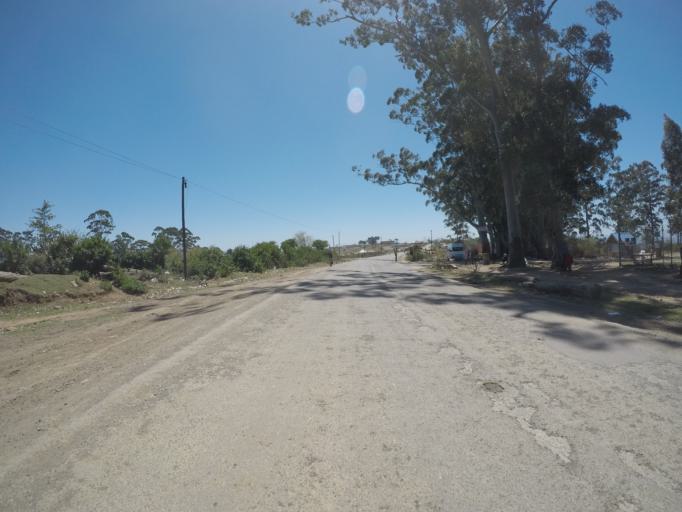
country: ZA
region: Eastern Cape
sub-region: OR Tambo District Municipality
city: Libode
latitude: -31.9186
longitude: 29.0308
